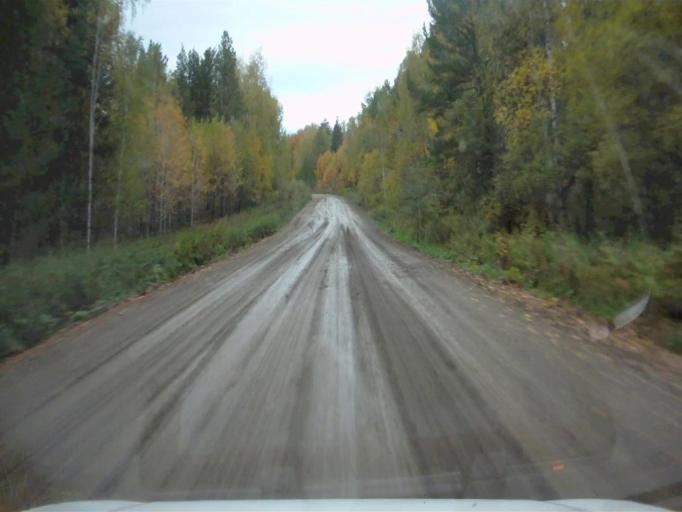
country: RU
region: Chelyabinsk
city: Nyazepetrovsk
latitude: 56.1185
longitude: 59.3690
